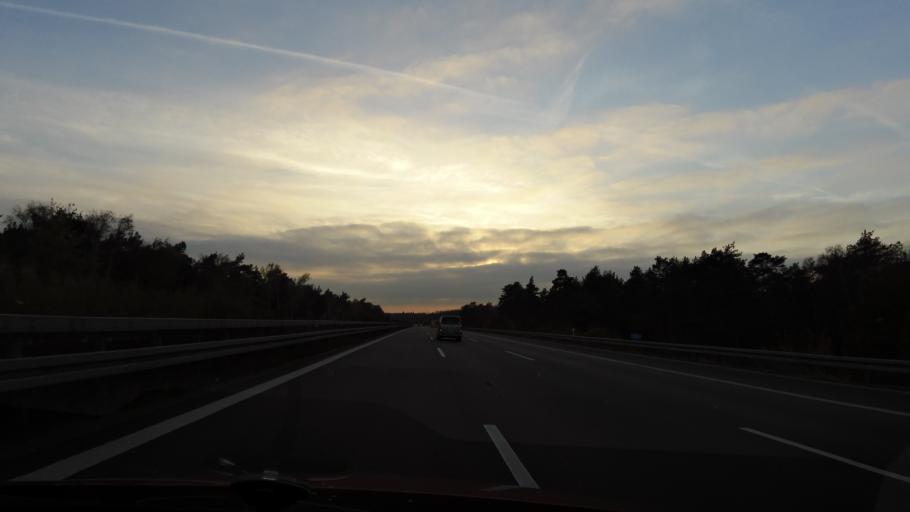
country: DE
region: Saxony-Anhalt
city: Raguhn
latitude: 51.7693
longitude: 12.2454
